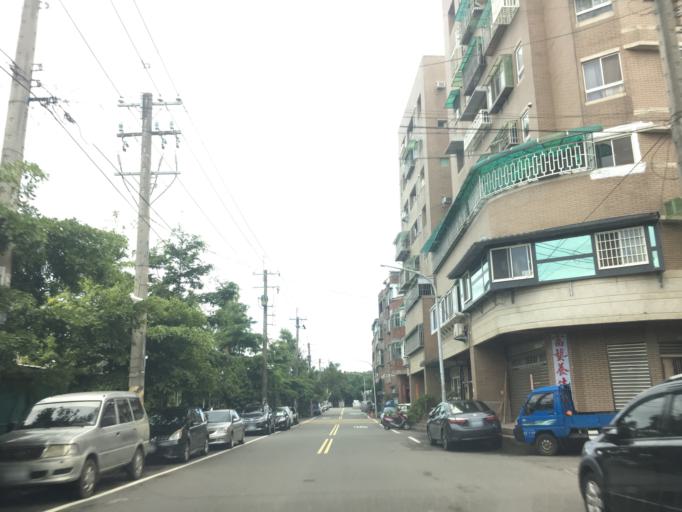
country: TW
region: Taiwan
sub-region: Yunlin
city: Douliu
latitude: 23.5887
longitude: 120.5501
